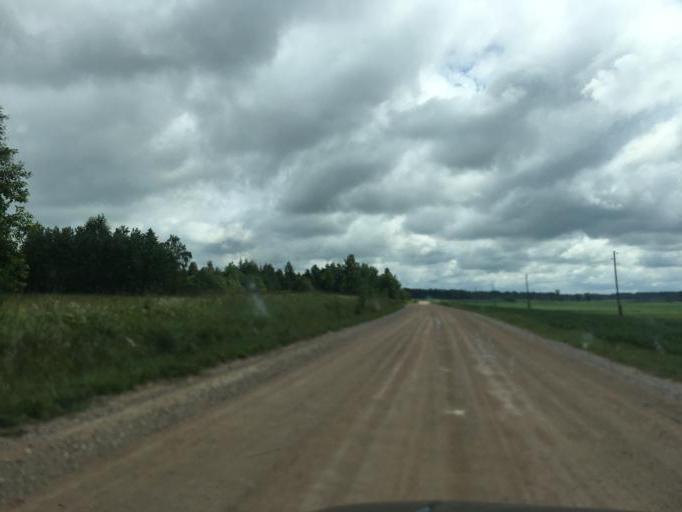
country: LV
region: Balvu Rajons
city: Balvi
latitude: 57.3392
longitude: 27.3414
